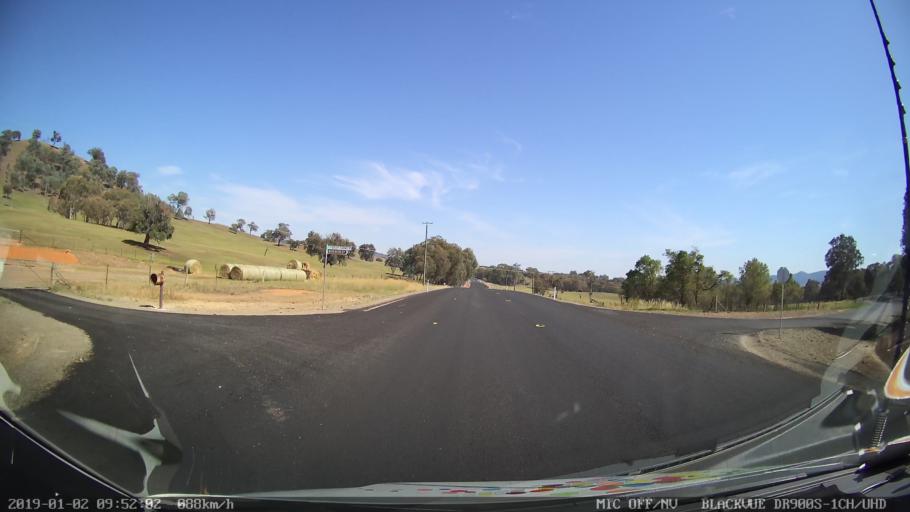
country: AU
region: New South Wales
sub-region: Tumut Shire
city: Tumut
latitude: -35.2656
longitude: 148.2094
